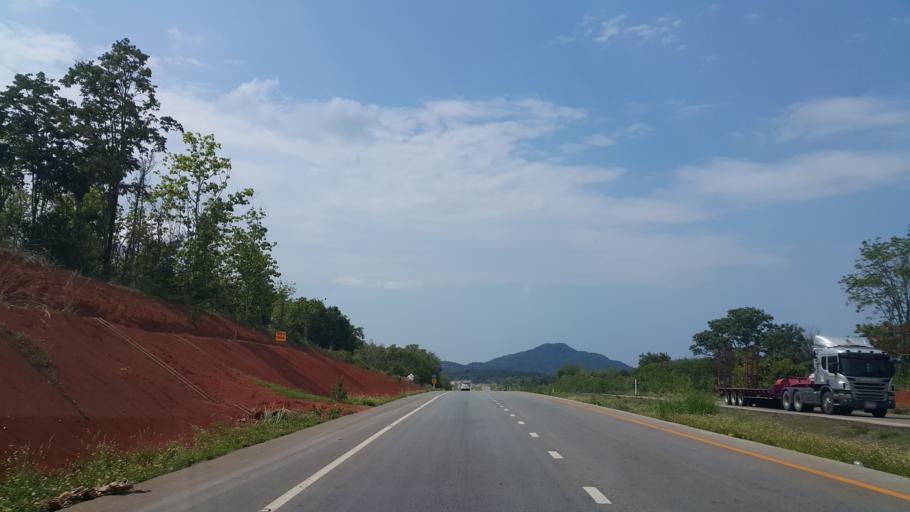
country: TH
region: Chiang Rai
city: Chiang Rai
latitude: 19.9943
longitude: 99.8920
